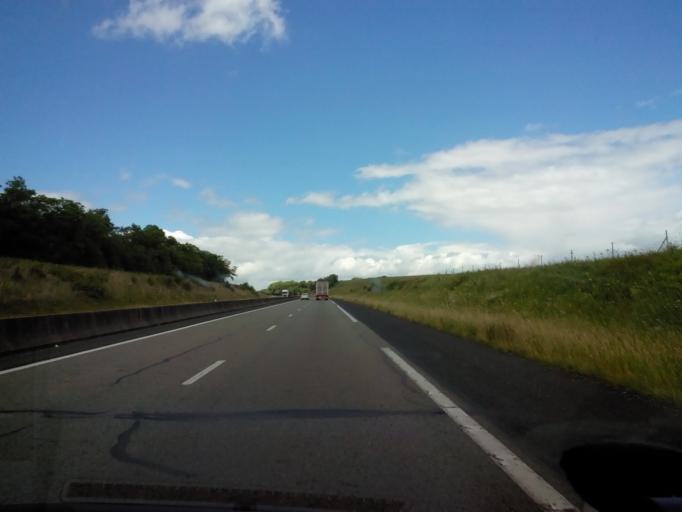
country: FR
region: Lorraine
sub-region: Departement des Vosges
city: Lamarche
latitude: 48.1047
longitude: 5.6503
